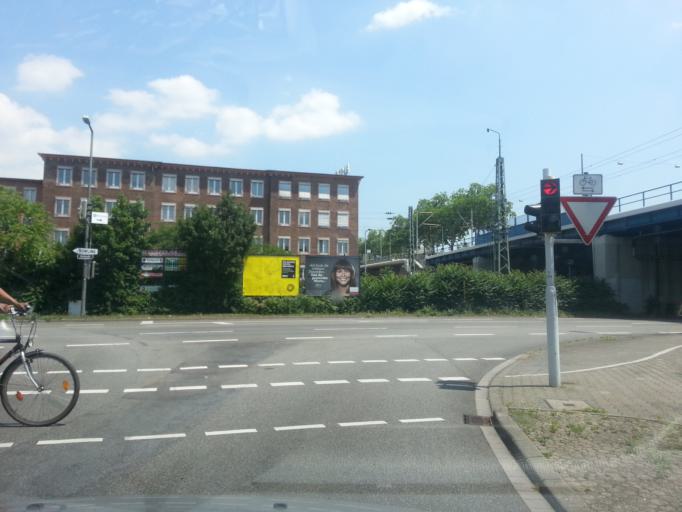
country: DE
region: Baden-Wuerttemberg
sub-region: Karlsruhe Region
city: Mannheim
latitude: 49.5049
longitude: 8.5006
